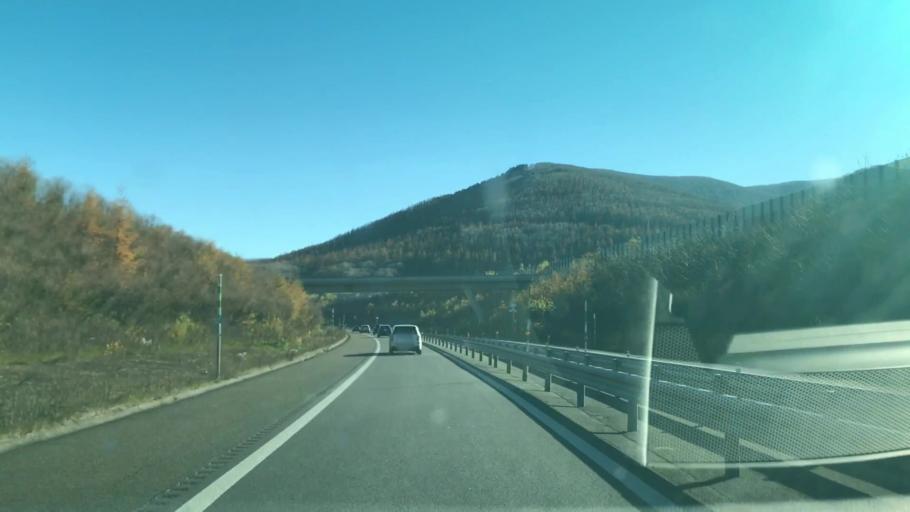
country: JP
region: Hokkaido
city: Otofuke
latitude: 43.0421
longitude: 142.7837
